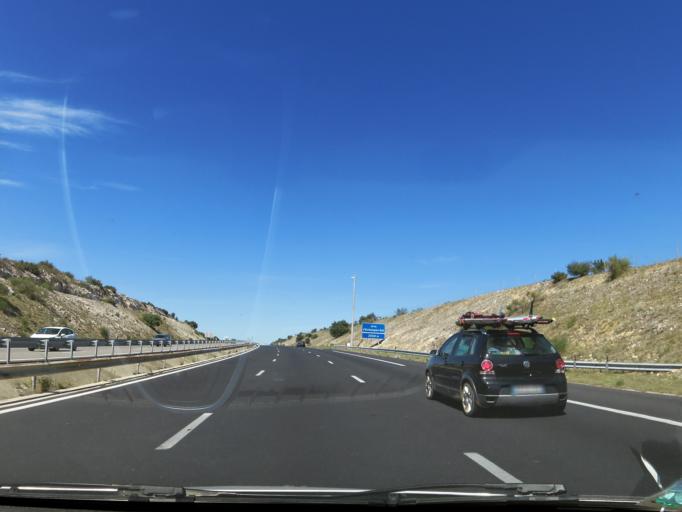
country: FR
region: Languedoc-Roussillon
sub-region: Departement du Gard
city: Remoulins
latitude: 43.9465
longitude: 4.6187
